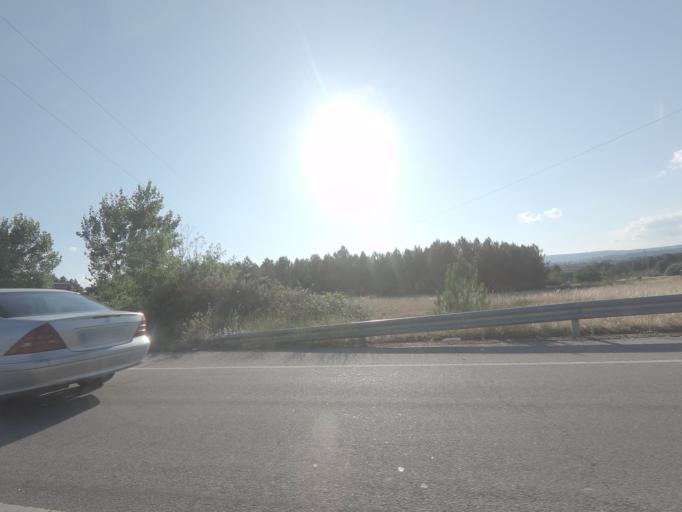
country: PT
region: Vila Real
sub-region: Chaves
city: Chaves
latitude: 41.8037
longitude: -7.4194
